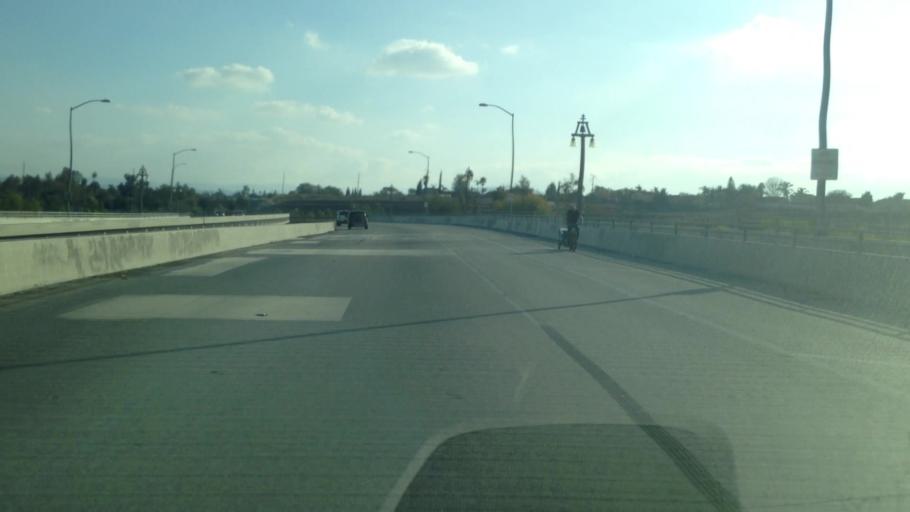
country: US
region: California
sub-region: Riverside County
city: Pedley
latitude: 33.9641
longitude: -117.4658
